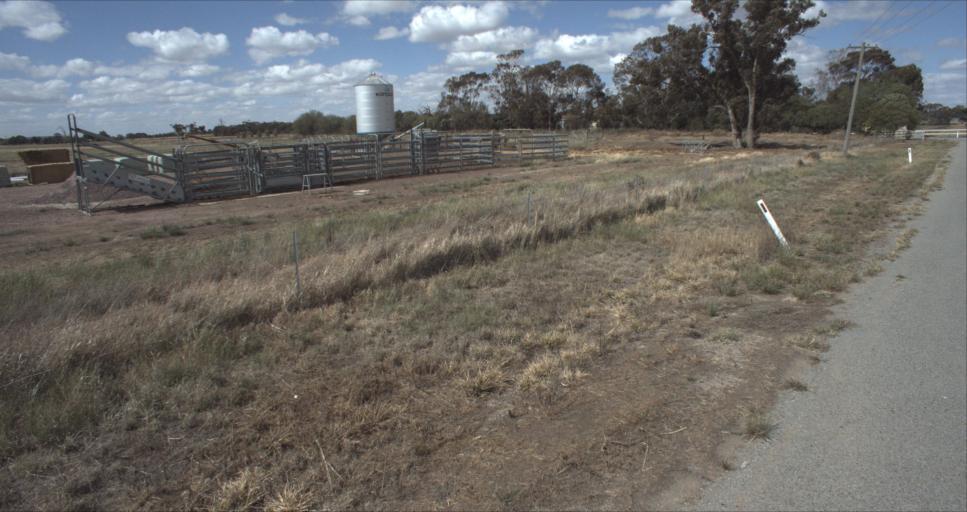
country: AU
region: New South Wales
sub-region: Leeton
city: Leeton
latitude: -34.5931
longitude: 146.4173
